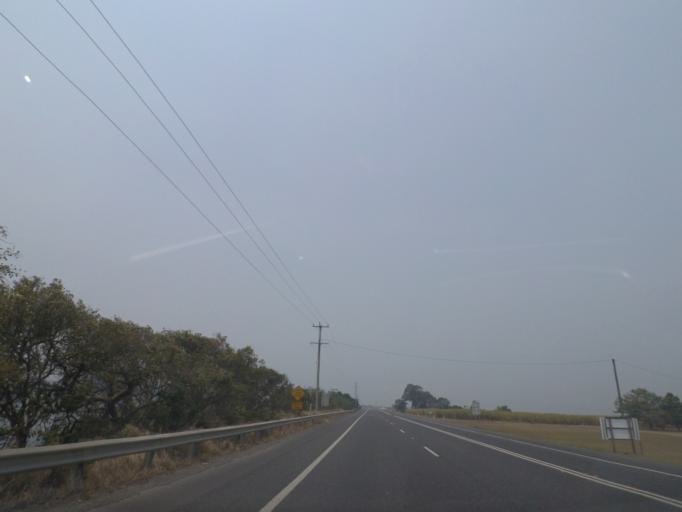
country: AU
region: New South Wales
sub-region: Richmond Valley
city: Evans Head
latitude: -28.9971
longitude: 153.4515
